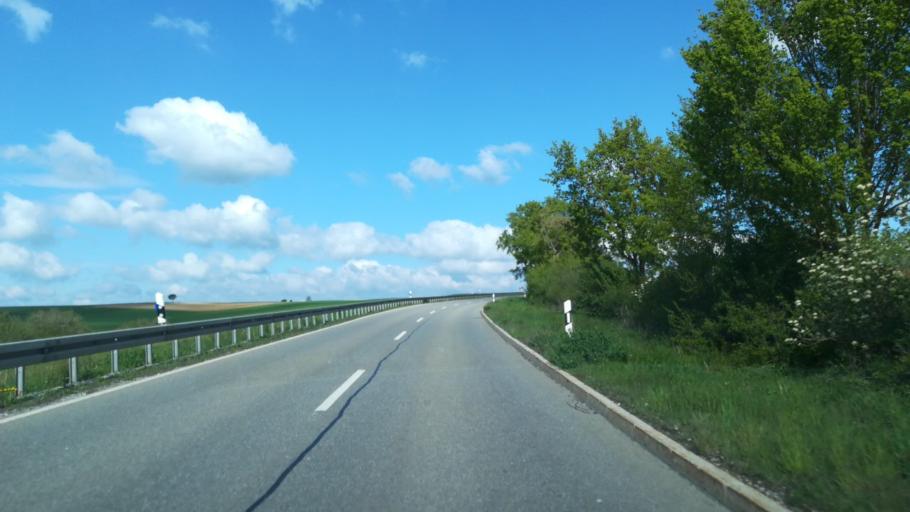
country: DE
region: Baden-Wuerttemberg
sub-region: Freiburg Region
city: Eggingen
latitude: 47.7585
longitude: 8.3849
